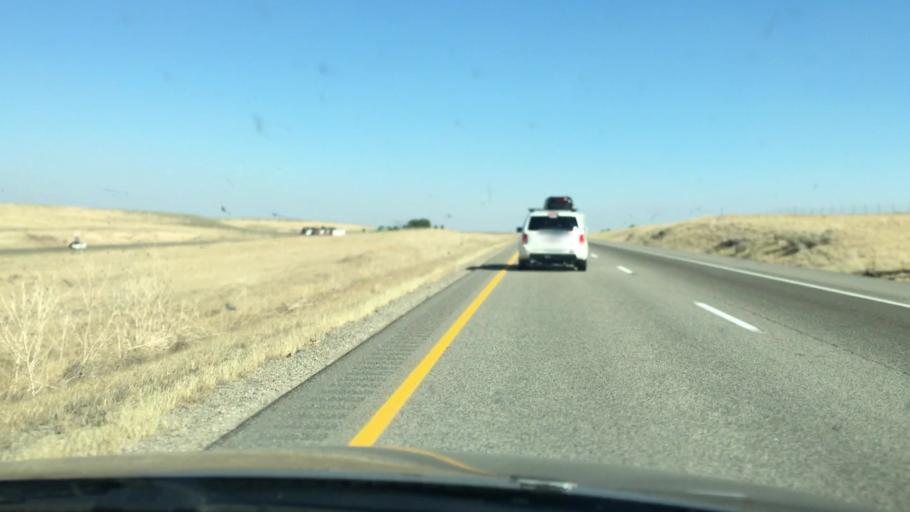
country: US
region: Idaho
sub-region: Ada County
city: Boise
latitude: 43.4834
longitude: -116.1153
